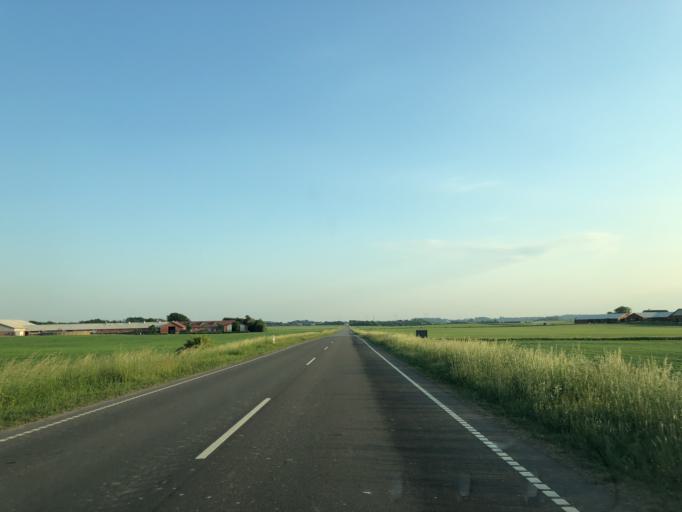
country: DK
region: Central Jutland
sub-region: Struer Kommune
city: Struer
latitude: 56.4592
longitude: 8.5430
